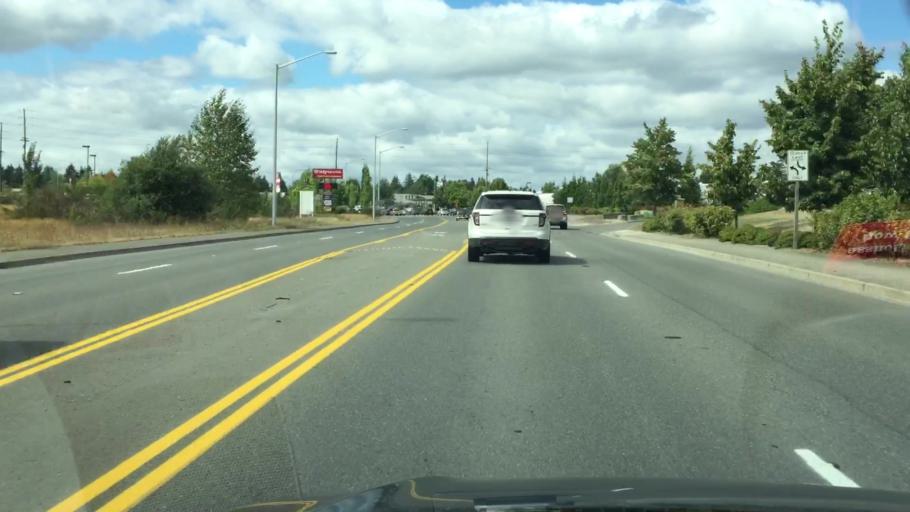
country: US
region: Washington
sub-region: Pierce County
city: Graham
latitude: 47.0979
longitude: -122.2901
